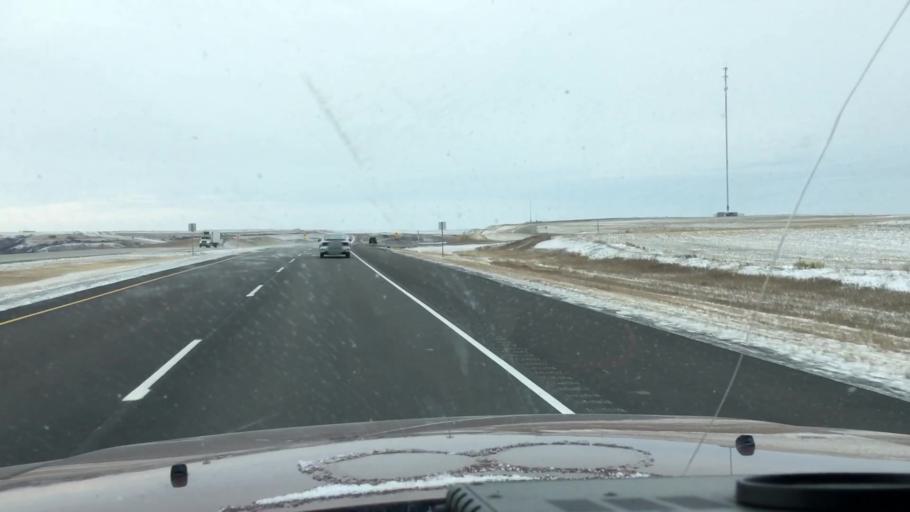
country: CA
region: Saskatchewan
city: Saskatoon
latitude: 51.7409
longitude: -106.4763
